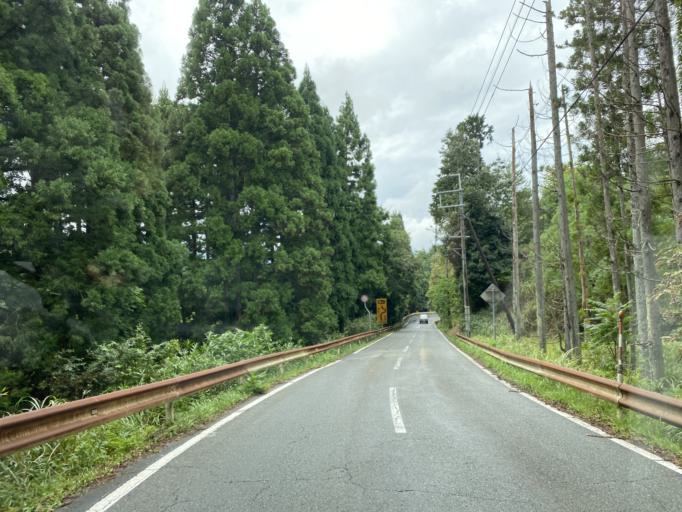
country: JP
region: Kyoto
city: Fukuchiyama
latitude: 35.3042
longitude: 134.9273
